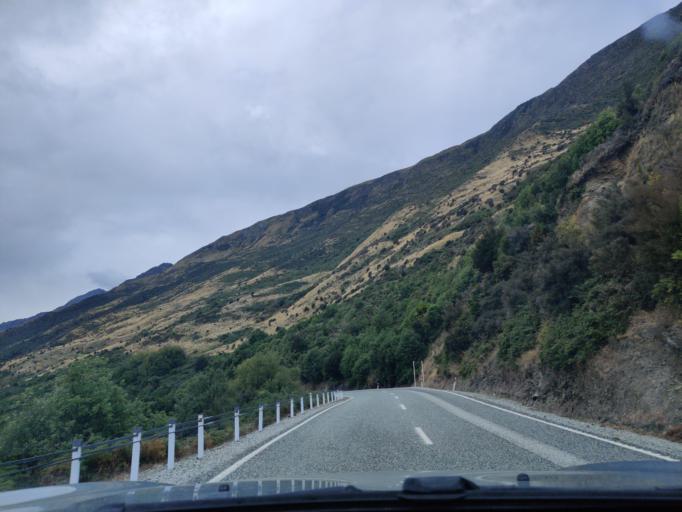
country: NZ
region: Otago
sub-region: Queenstown-Lakes District
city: Wanaka
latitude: -44.3372
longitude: 169.1783
